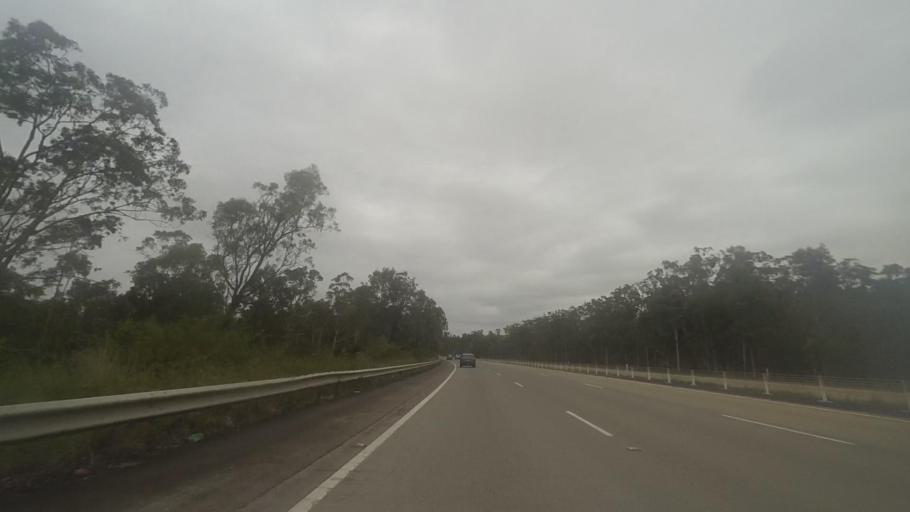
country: AU
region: New South Wales
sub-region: Port Stephens Shire
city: Medowie
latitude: -32.6867
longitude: 151.8102
